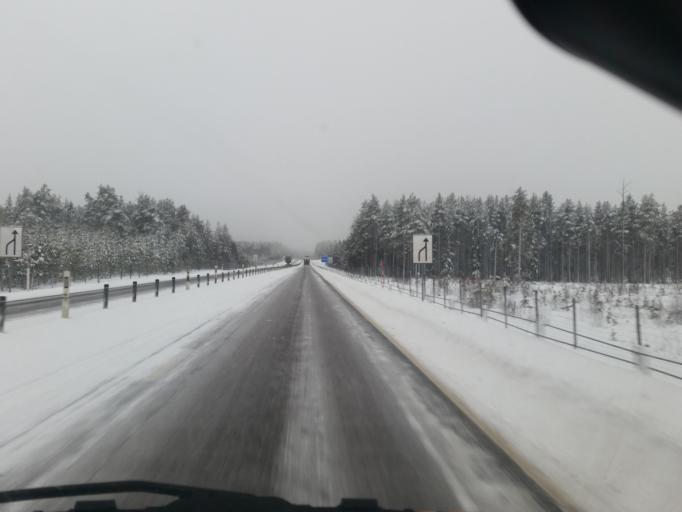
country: SE
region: Norrbotten
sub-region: Pitea Kommun
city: Pitea
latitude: 65.1840
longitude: 21.5057
